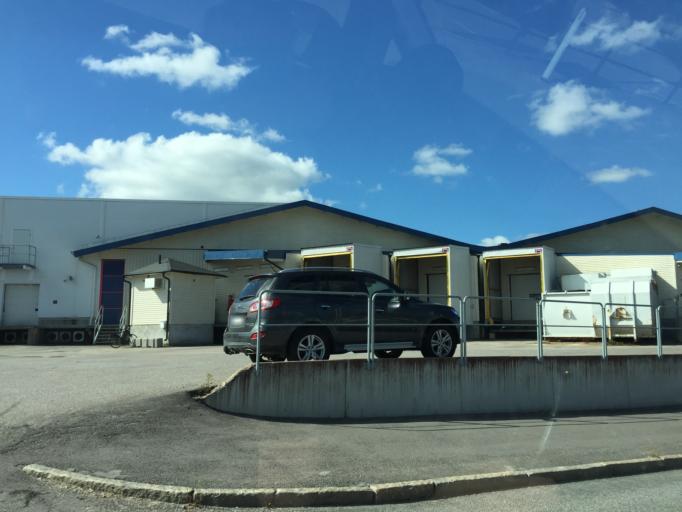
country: SE
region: Soedermanland
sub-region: Katrineholms Kommun
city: Katrineholm
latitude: 59.0026
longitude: 16.2264
